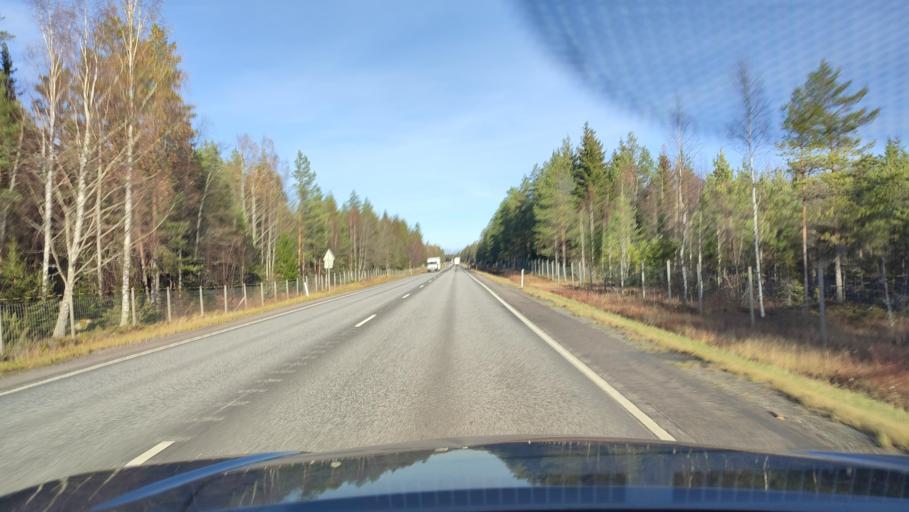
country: FI
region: Ostrobothnia
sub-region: Vaasa
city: Malax
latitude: 62.8261
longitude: 21.6906
